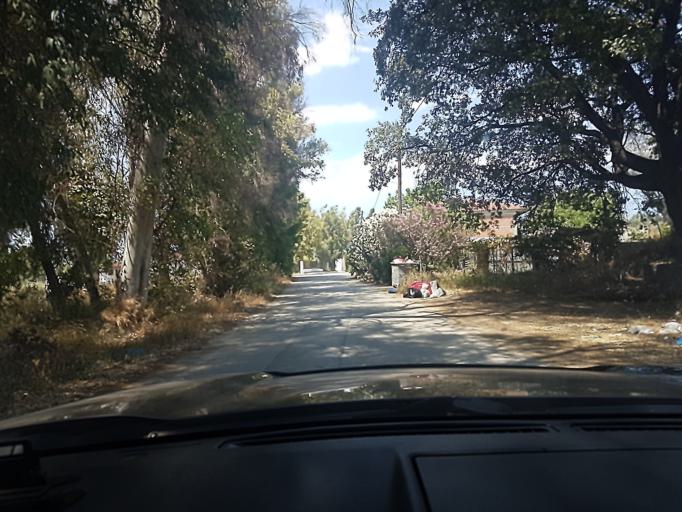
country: GR
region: Central Greece
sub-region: Nomos Evvoias
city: Vasilikon
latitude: 38.4209
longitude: 23.6625
